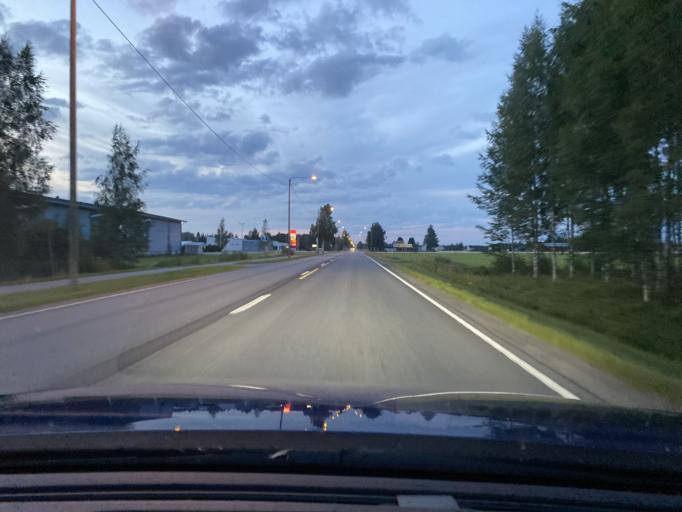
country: FI
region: Southern Ostrobothnia
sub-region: Suupohja
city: Kauhajoki
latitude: 62.4280
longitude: 22.2028
